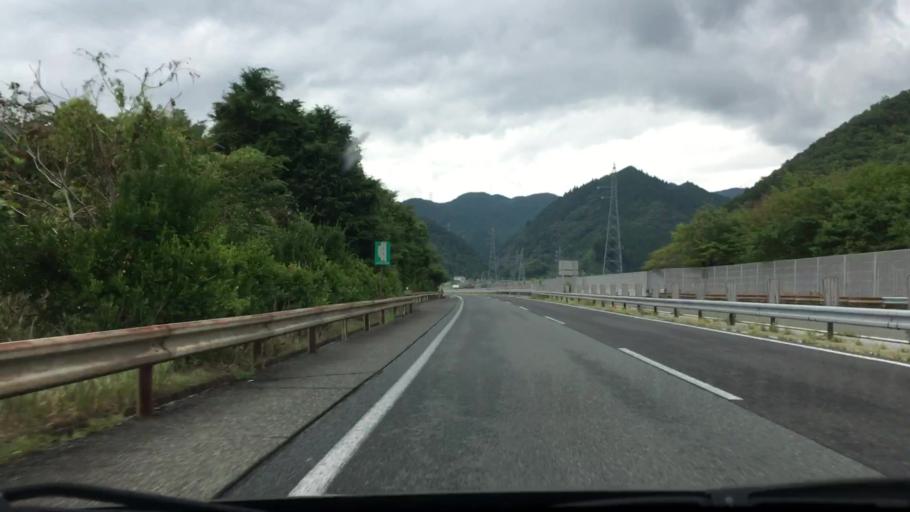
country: JP
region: Okayama
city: Niimi
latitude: 35.0053
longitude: 133.4402
